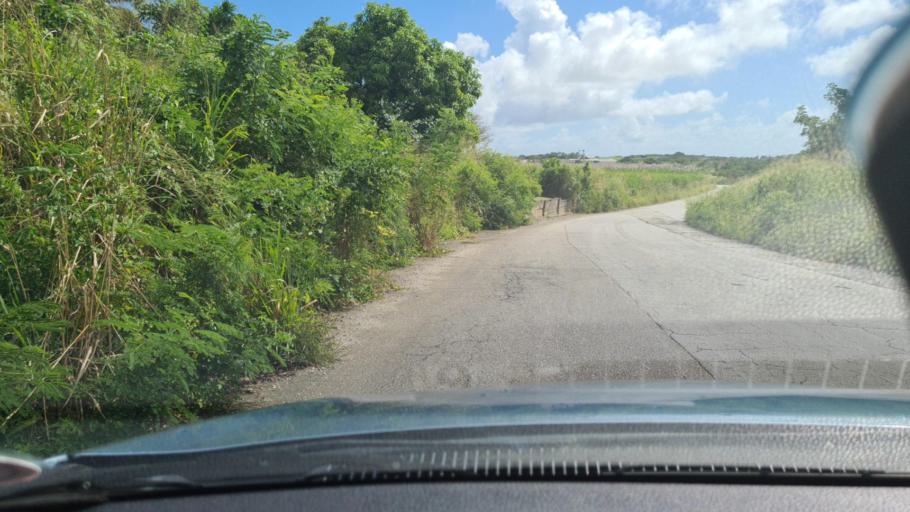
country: BB
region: Christ Church
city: Oistins
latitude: 13.0885
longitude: -59.5436
